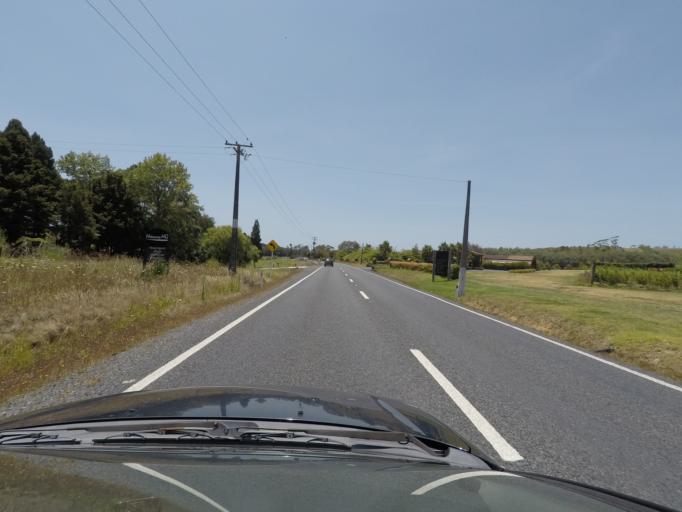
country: NZ
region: Auckland
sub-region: Auckland
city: Warkworth
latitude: -36.3733
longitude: 174.6787
